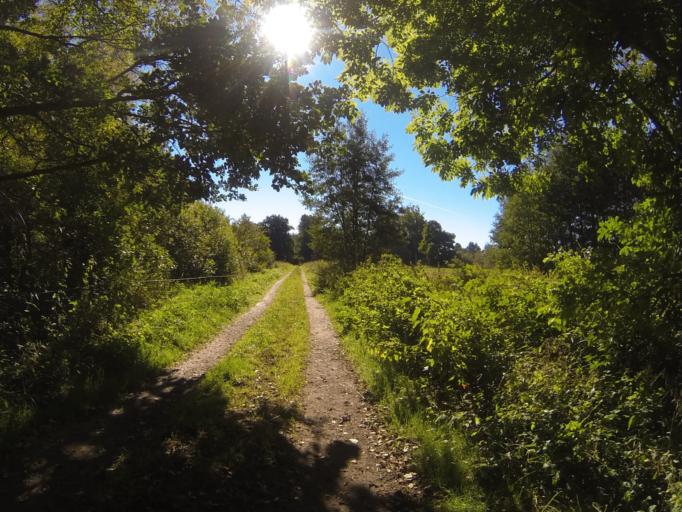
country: SE
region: Skane
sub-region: Hoors Kommun
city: Loberod
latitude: 55.7239
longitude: 13.4072
